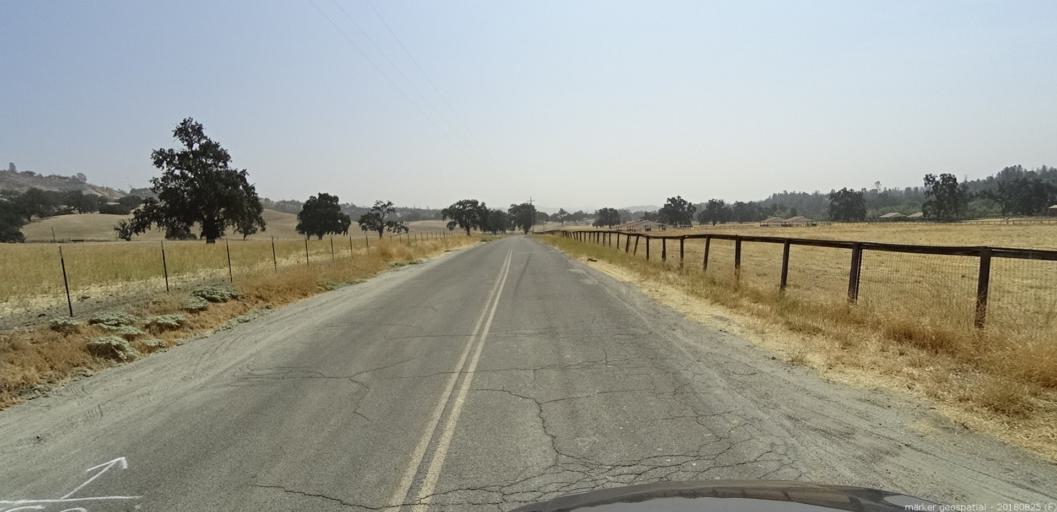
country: US
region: California
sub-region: Fresno County
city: Coalinga
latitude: 35.9112
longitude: -120.4716
